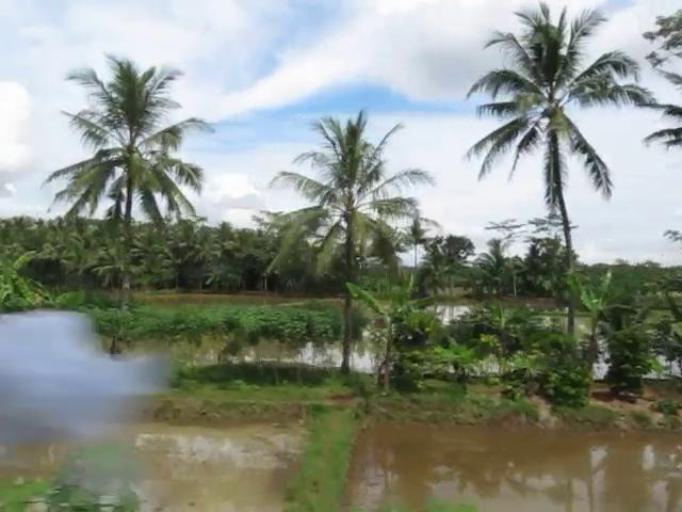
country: ID
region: Central Java
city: Meluwung
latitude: -7.3863
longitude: 108.6950
